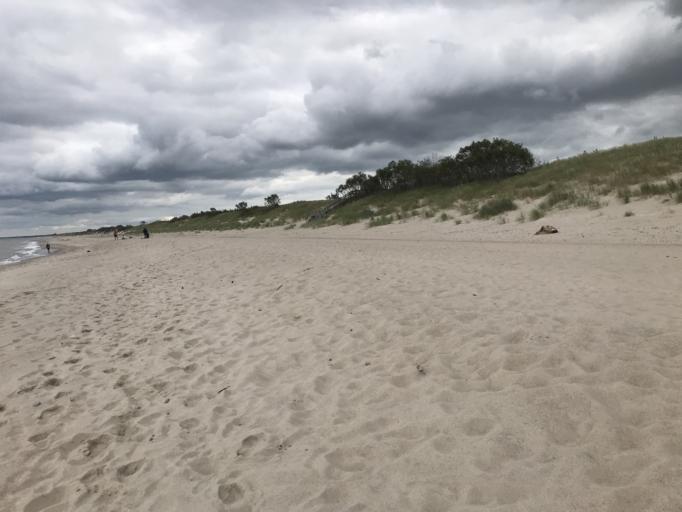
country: LT
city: Nida
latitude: 55.2486
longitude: 20.9203
